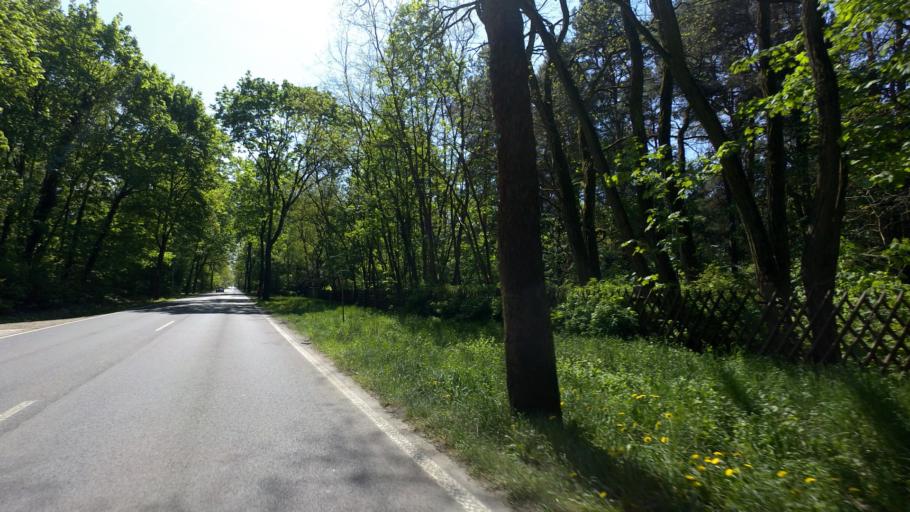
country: DE
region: Brandenburg
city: Bestensee
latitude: 52.2564
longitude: 13.6538
